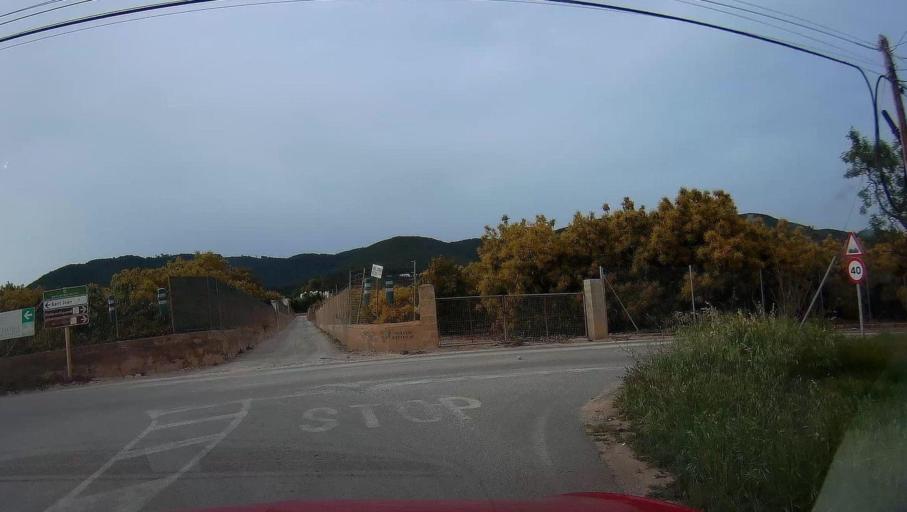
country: ES
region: Balearic Islands
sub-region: Illes Balears
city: Sant Joan de Labritja
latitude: 39.0376
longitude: 1.5429
